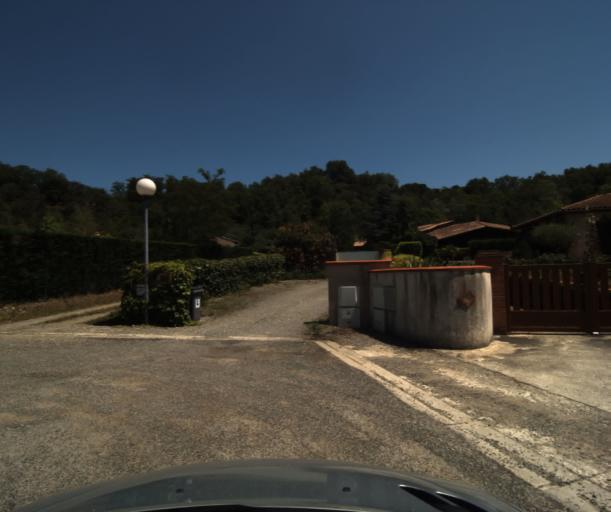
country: FR
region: Midi-Pyrenees
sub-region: Departement de la Haute-Garonne
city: Muret
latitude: 43.4717
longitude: 1.3435
